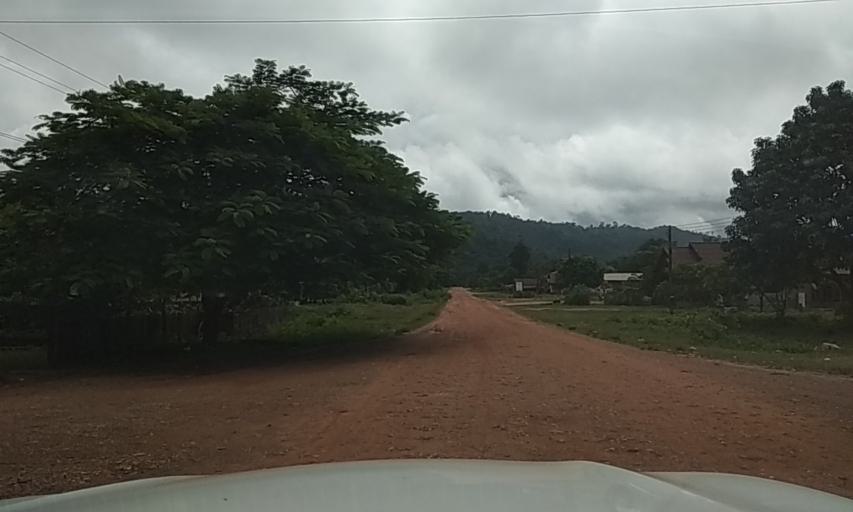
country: LA
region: Bolikhamxai
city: Bolikhan
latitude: 18.5571
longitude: 103.7364
